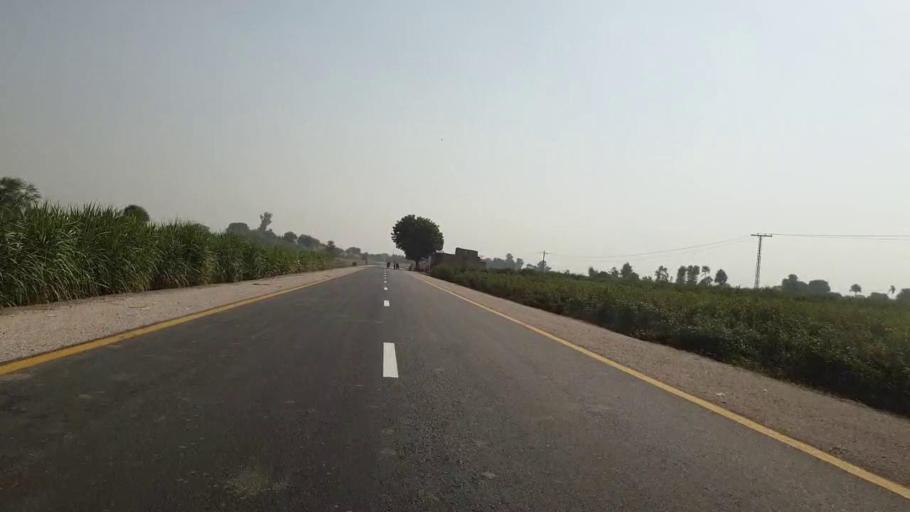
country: PK
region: Sindh
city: Bhan
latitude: 26.6059
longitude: 67.7791
